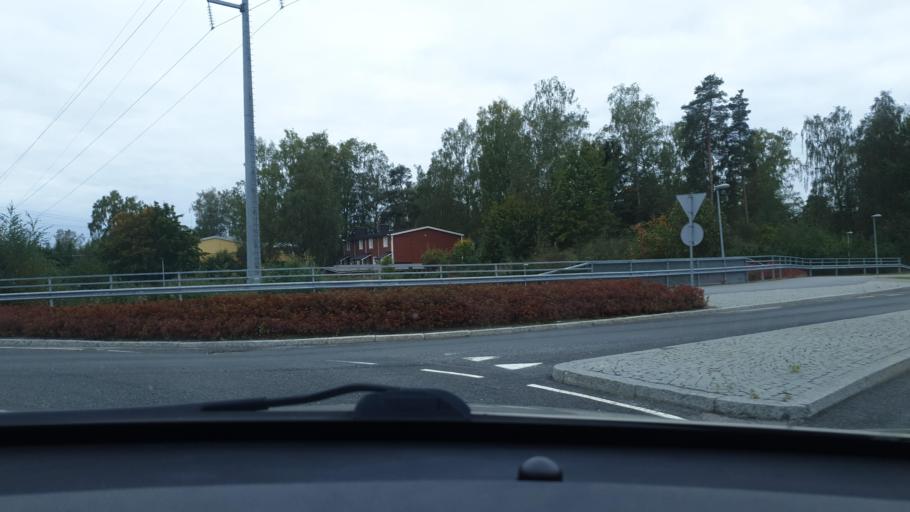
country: FI
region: Ostrobothnia
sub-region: Vaasa
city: Korsholm
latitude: 63.0991
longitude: 21.6609
